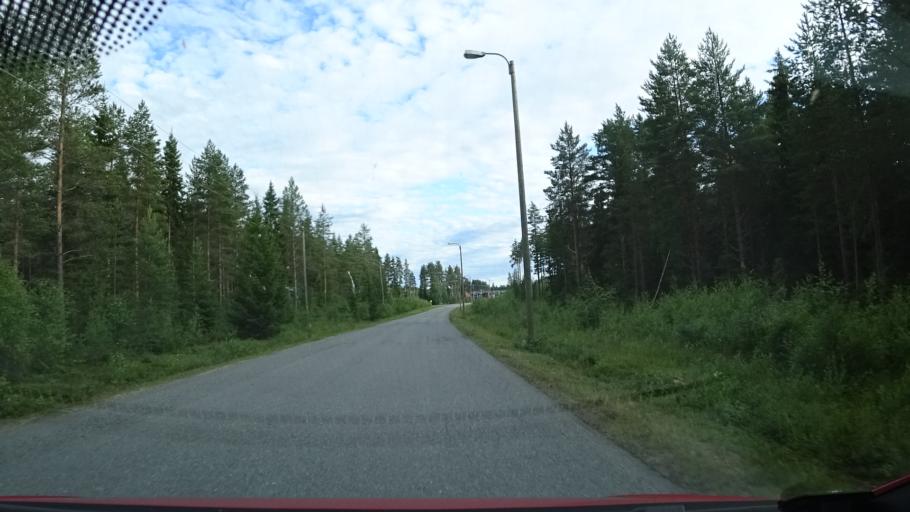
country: FI
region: Northern Ostrobothnia
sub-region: Oulu
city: Haukipudas
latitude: 65.1996
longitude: 25.4134
